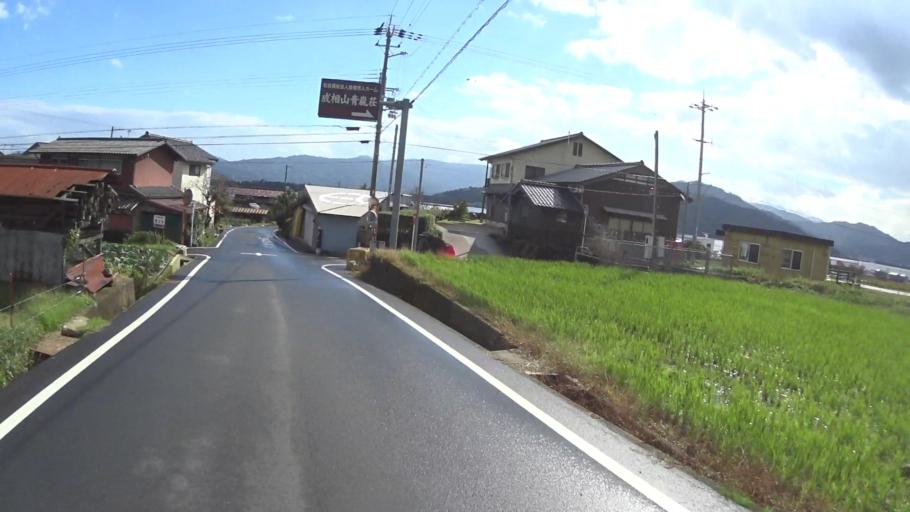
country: JP
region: Kyoto
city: Miyazu
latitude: 35.5783
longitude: 135.1792
